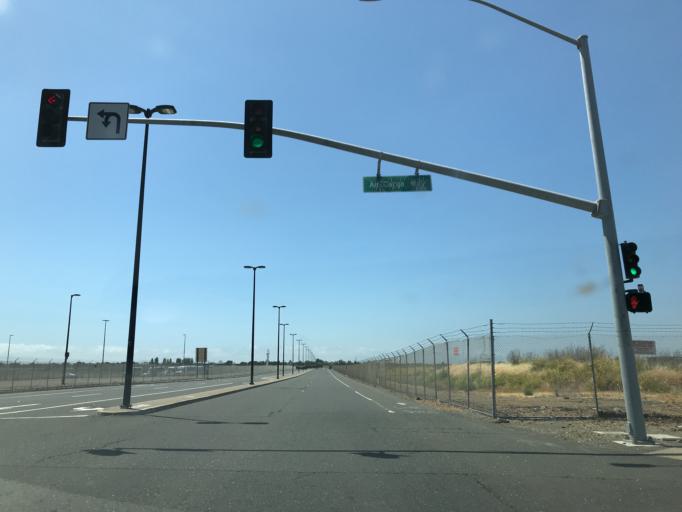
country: US
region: California
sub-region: Alameda County
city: Alameda
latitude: 37.7231
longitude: -122.2169
